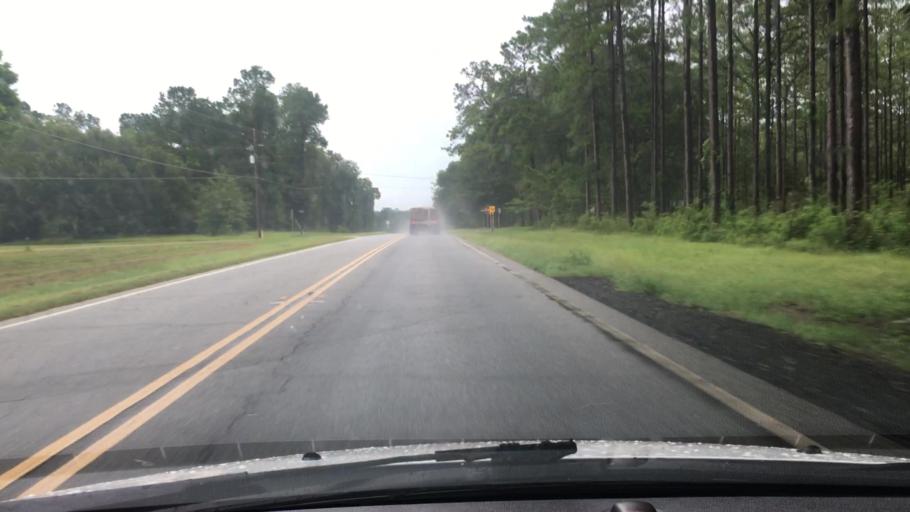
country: US
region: Georgia
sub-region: Grady County
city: Cairo
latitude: 30.7864
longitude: -84.2728
